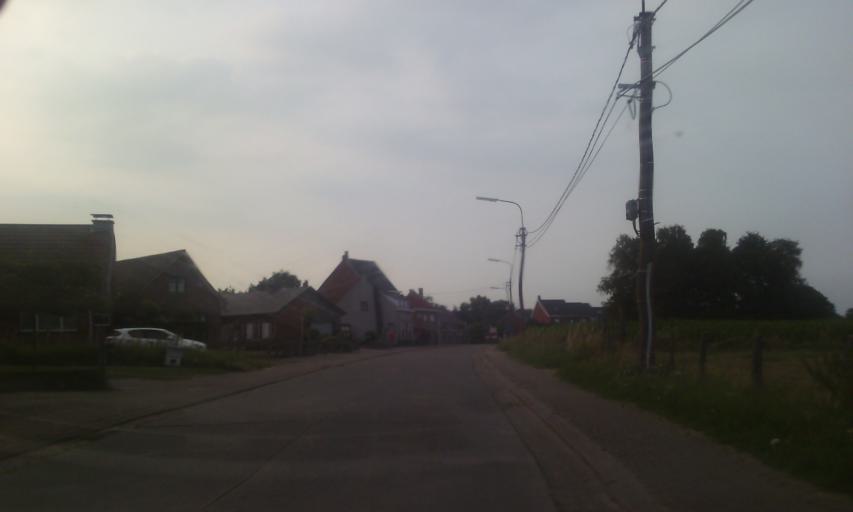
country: BE
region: Flanders
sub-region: Provincie Oost-Vlaanderen
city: Lede
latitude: 50.9776
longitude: 3.9571
